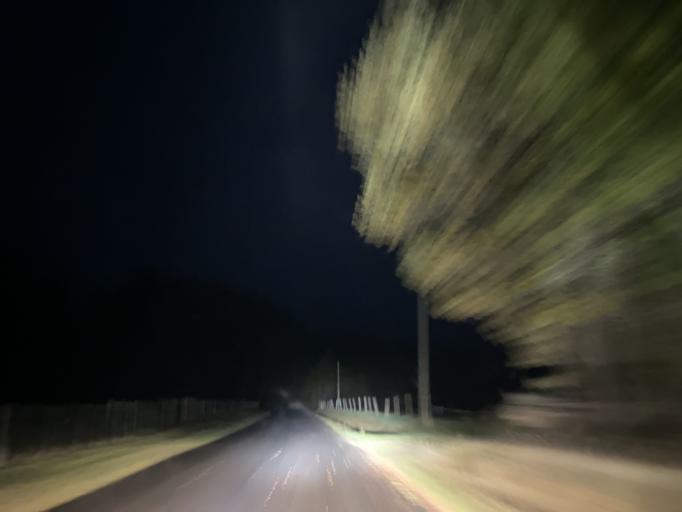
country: FR
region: Auvergne
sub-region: Departement du Puy-de-Dome
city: Cunlhat
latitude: 45.6207
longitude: 3.6428
